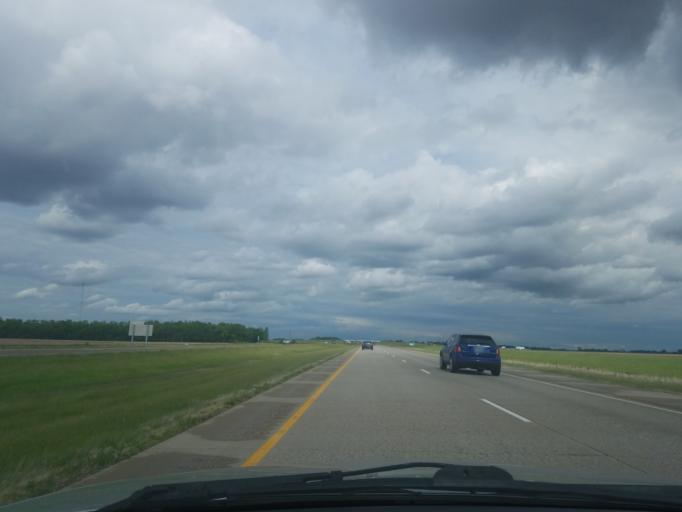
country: US
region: North Dakota
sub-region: Cass County
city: West Fargo
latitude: 46.8773
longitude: -97.0283
